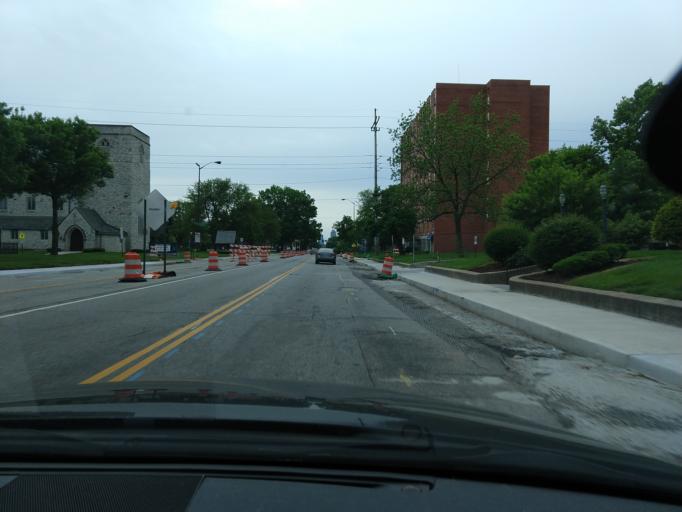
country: US
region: Indiana
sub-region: Marion County
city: Indianapolis
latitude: 39.8161
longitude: -86.1568
